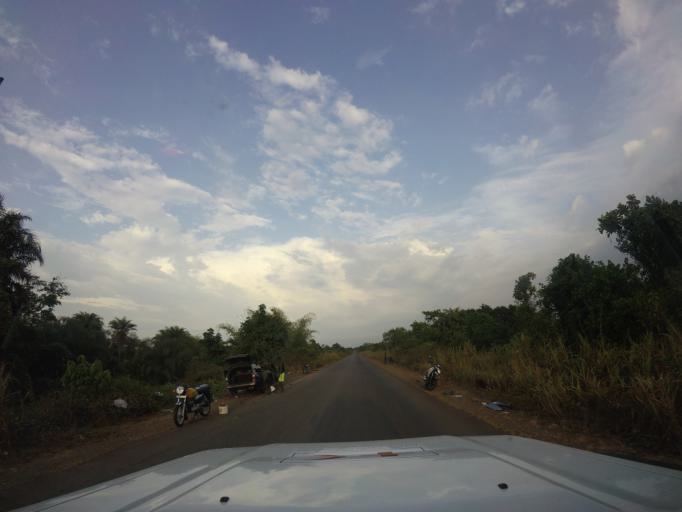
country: LR
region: Bomi
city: Tubmanburg
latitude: 6.7121
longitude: -10.9564
